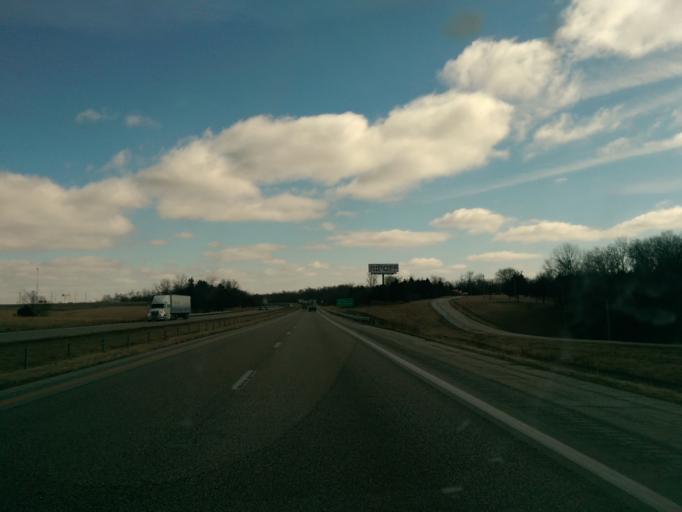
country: US
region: Missouri
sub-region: Montgomery County
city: Montgomery City
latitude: 38.8694
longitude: -91.3619
